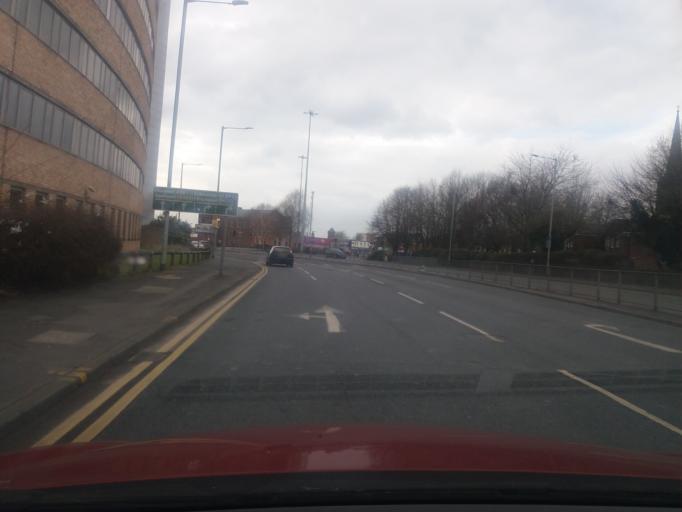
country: GB
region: England
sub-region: Lancashire
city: Preston
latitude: 53.7624
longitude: -2.6957
